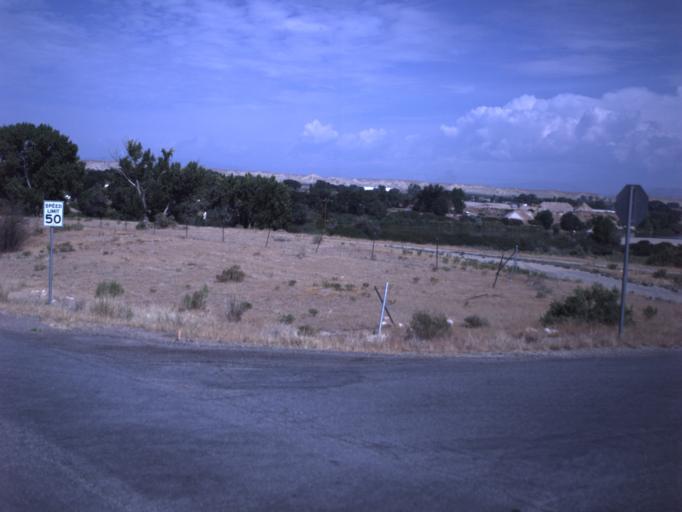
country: US
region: Utah
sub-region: Uintah County
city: Naples
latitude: 40.3696
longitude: -109.3312
